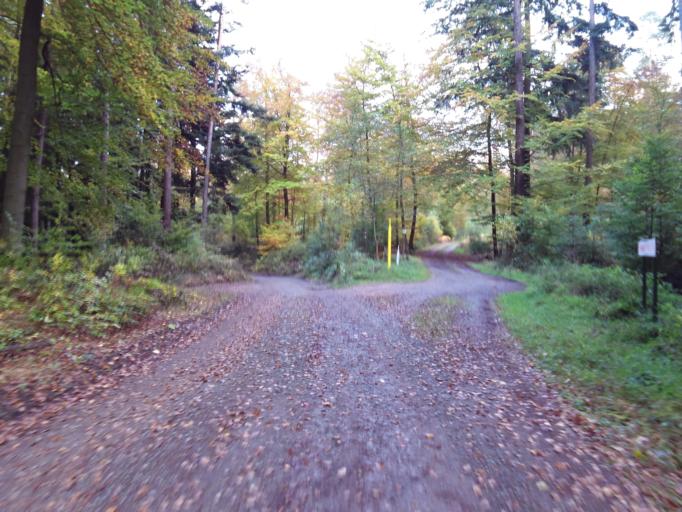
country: DE
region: Rheinland-Pfalz
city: Frankenstein
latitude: 49.4434
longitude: 8.0053
